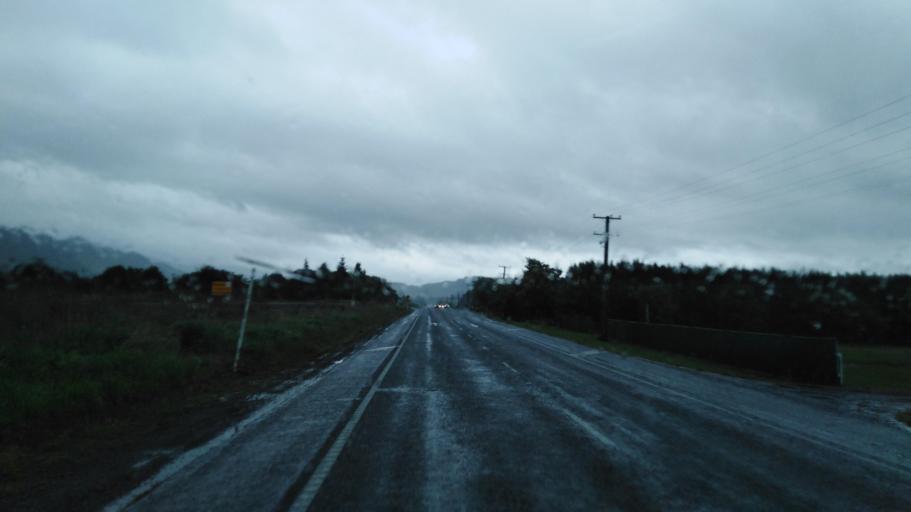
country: NZ
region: Manawatu-Wanganui
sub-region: Horowhenua District
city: Levin
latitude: -40.7029
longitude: 175.2219
